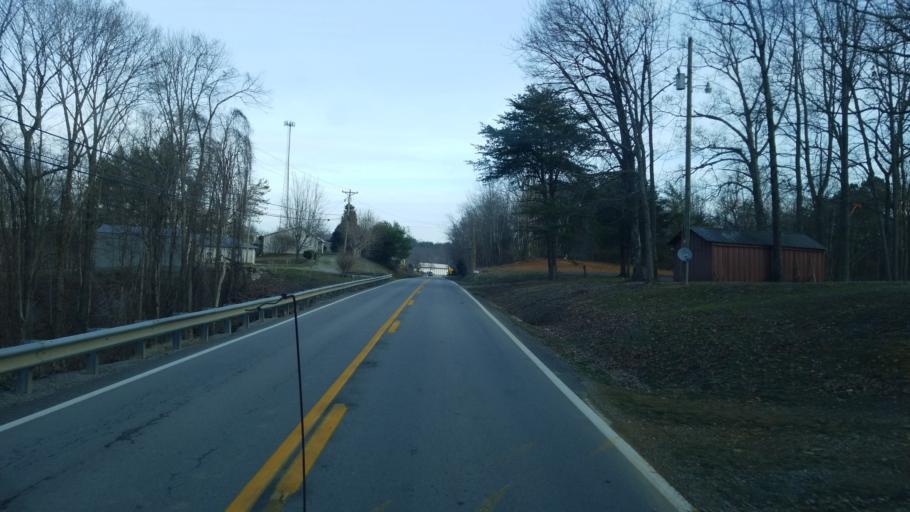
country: US
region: Kentucky
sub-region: Russell County
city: Jamestown
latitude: 36.8809
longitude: -85.1011
